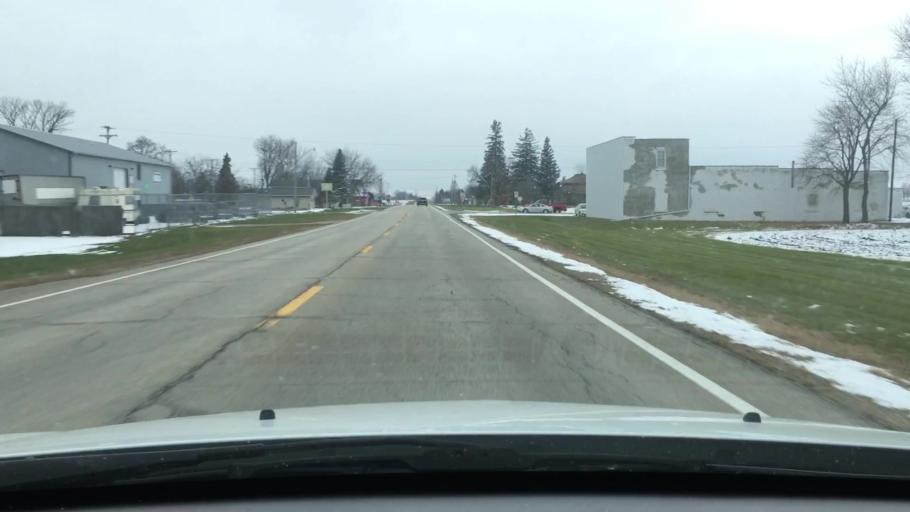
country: US
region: Illinois
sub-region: DeKalb County
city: Malta
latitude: 41.9358
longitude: -88.8594
